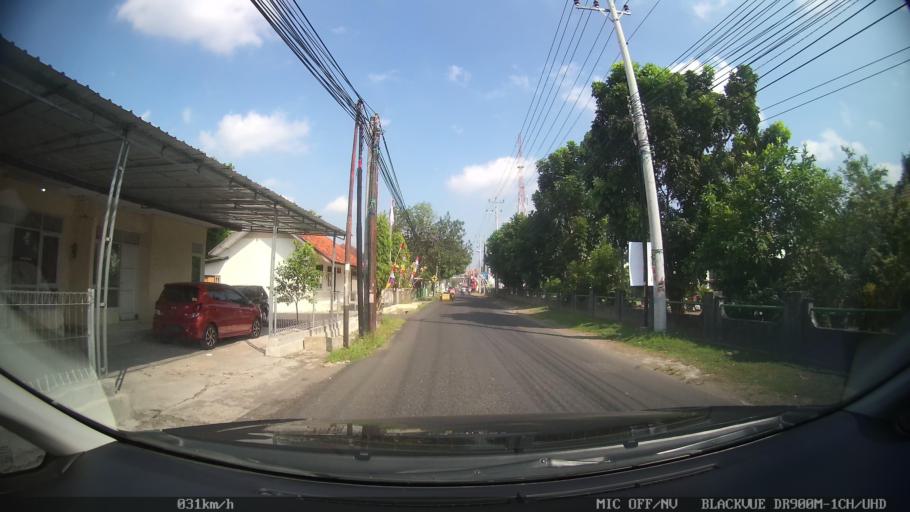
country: ID
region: Daerah Istimewa Yogyakarta
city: Melati
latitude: -7.7546
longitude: 110.3869
